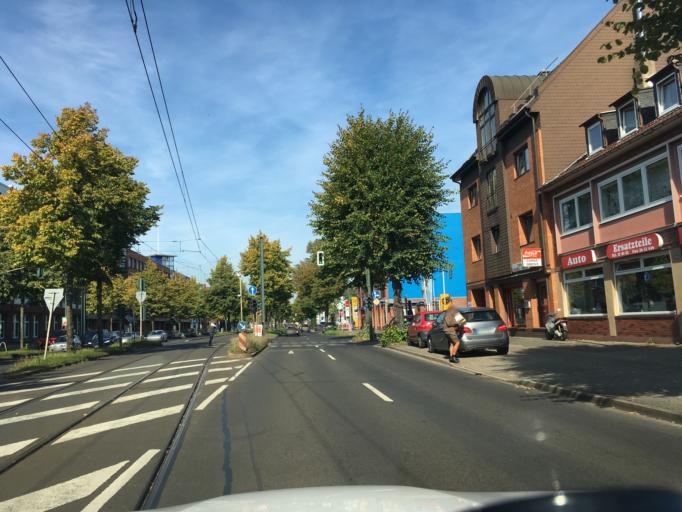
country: DE
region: North Rhine-Westphalia
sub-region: Regierungsbezirk Dusseldorf
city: Dusseldorf
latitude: 51.2119
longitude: 6.8256
